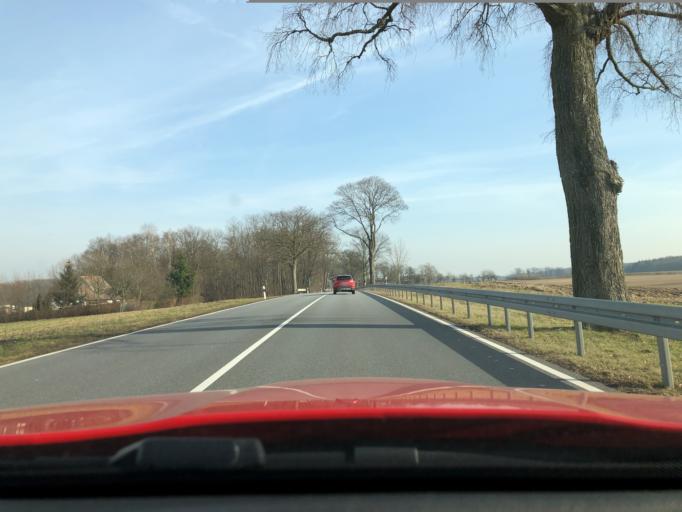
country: DE
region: Brandenburg
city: Muncheberg
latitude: 52.5055
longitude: 14.1964
